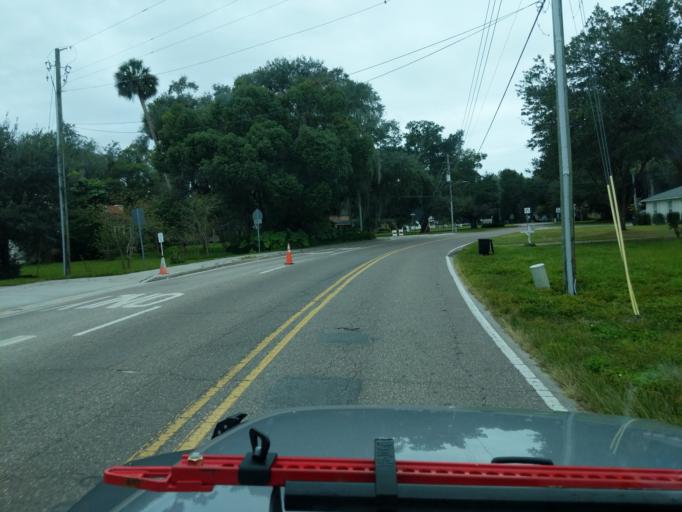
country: US
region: Florida
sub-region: Orange County
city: Oakland
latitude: 28.5548
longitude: -81.6238
